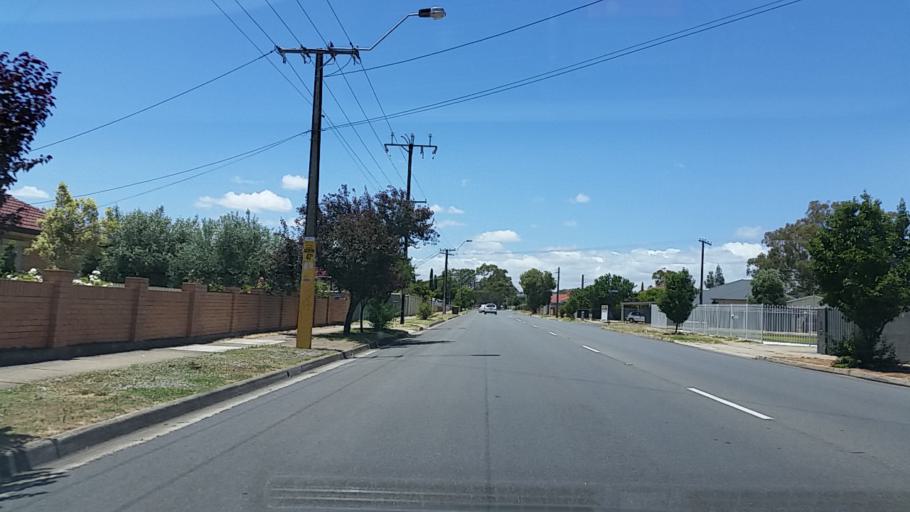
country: AU
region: South Australia
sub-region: Salisbury
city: Salisbury
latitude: -34.7633
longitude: 138.6358
